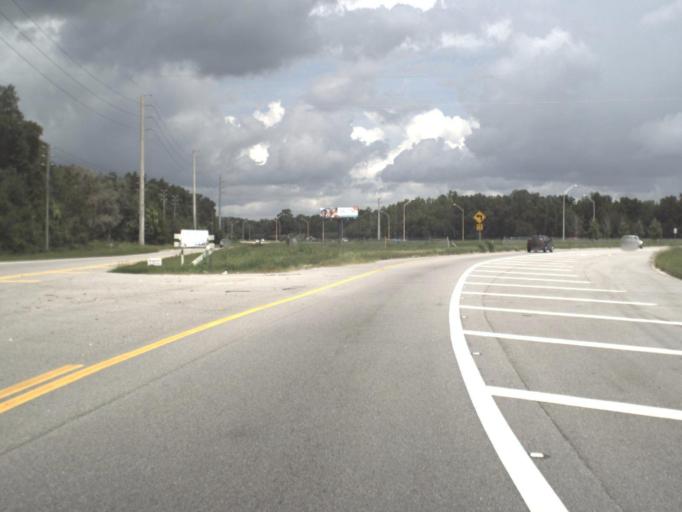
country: US
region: Florida
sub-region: Pasco County
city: Wesley Chapel
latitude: 28.2356
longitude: -82.3048
